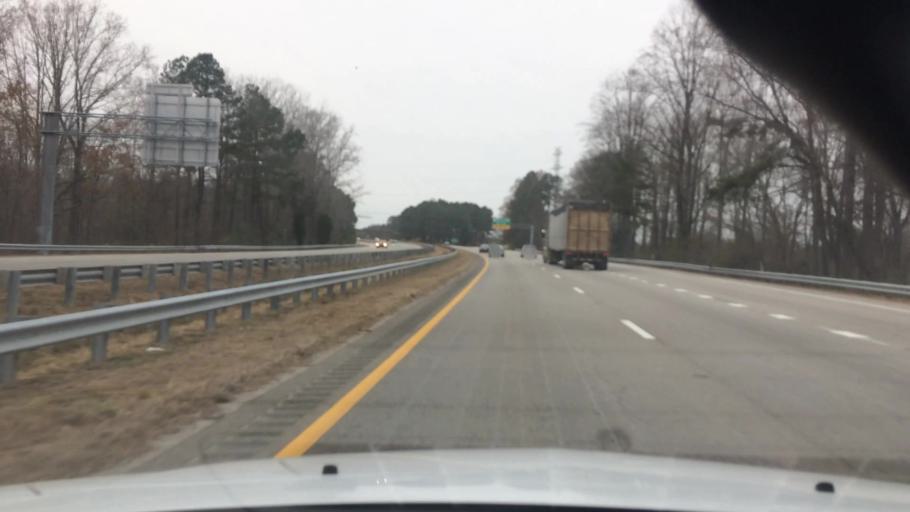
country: US
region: North Carolina
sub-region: Nash County
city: Red Oak
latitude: 35.9826
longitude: -77.8913
